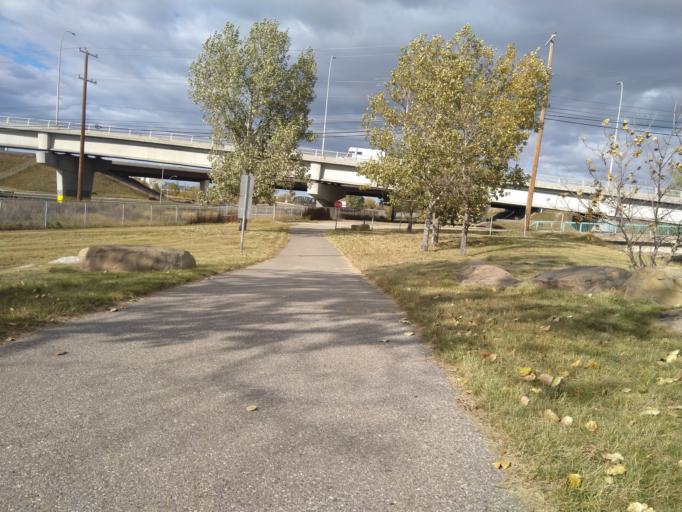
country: CA
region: Alberta
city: Calgary
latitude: 51.0082
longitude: -114.0098
